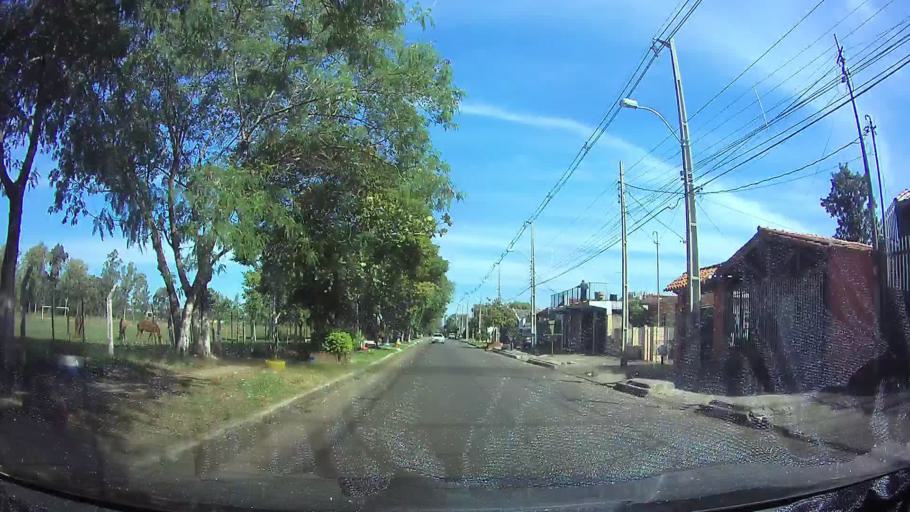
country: PY
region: Central
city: Colonia Mariano Roque Alonso
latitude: -25.2447
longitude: -57.5449
